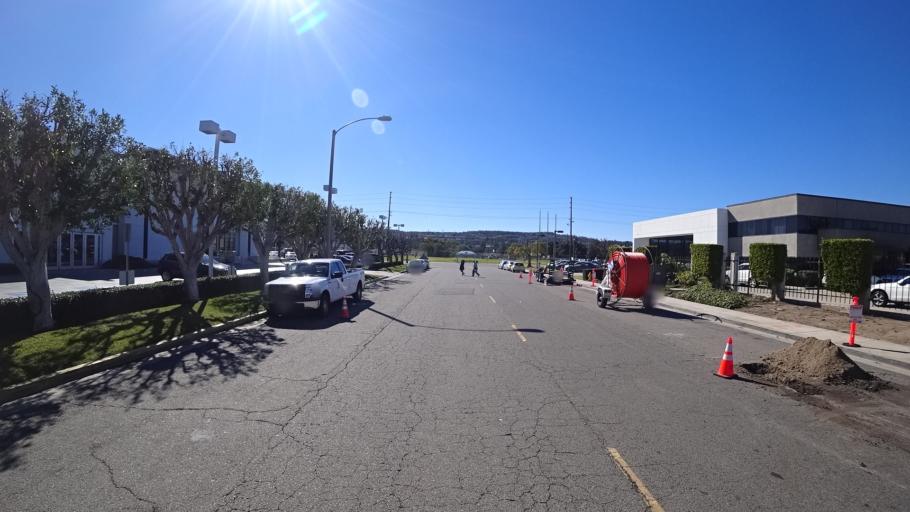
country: US
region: California
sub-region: Orange County
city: Yorba Linda
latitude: 33.8603
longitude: -117.7990
